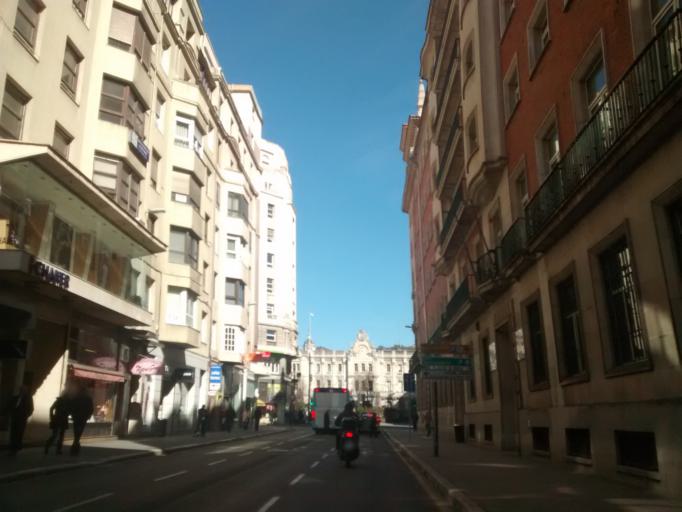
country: ES
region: Cantabria
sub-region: Provincia de Cantabria
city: Santander
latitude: 43.4607
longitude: -3.8092
